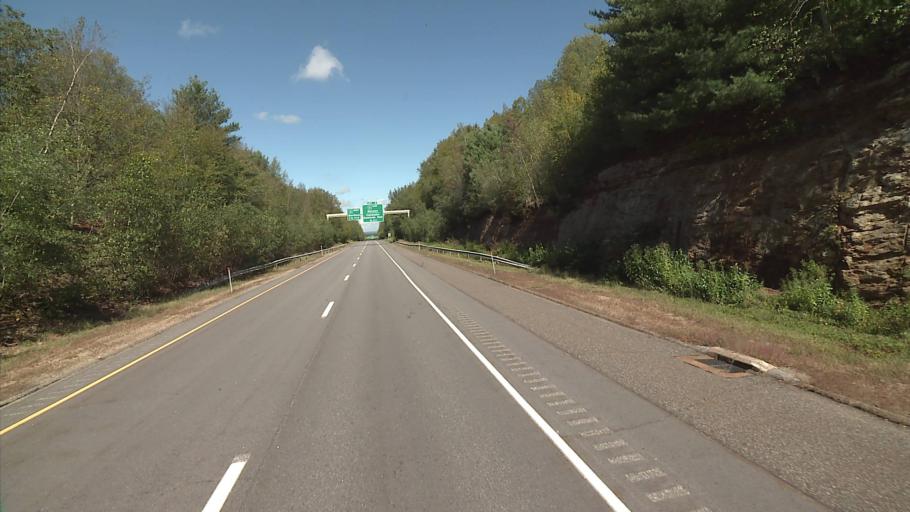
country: US
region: Connecticut
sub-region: New London County
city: Colchester
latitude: 41.5475
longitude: -72.3162
